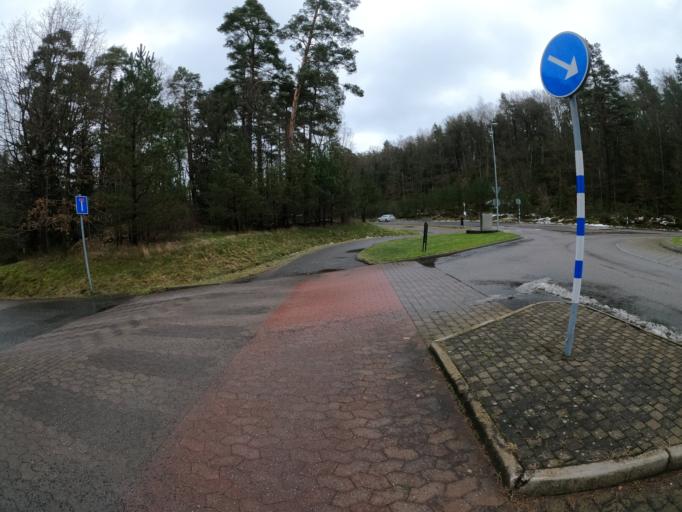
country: SE
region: Vaestra Goetaland
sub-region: Harryda Kommun
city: Molnlycke
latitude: 57.6430
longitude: 12.1128
